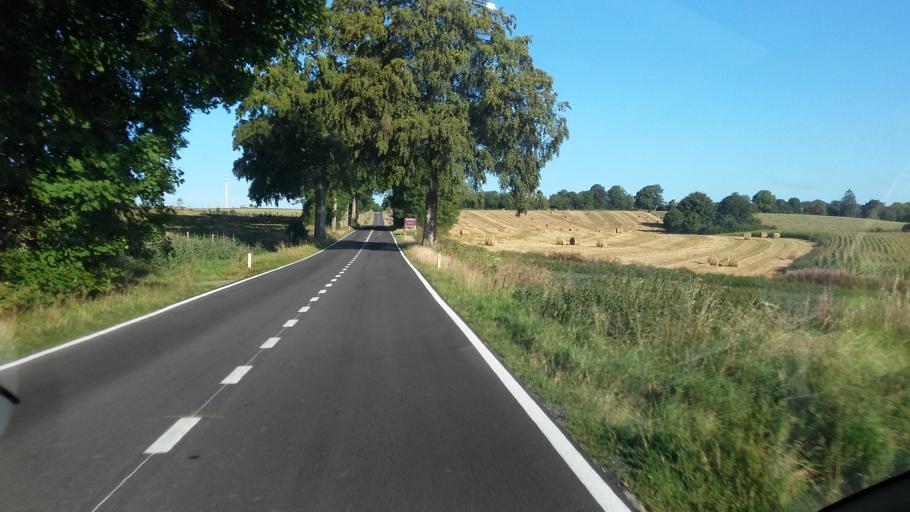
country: BE
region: Wallonia
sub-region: Province du Luxembourg
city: Leglise
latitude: 49.8206
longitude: 5.4943
